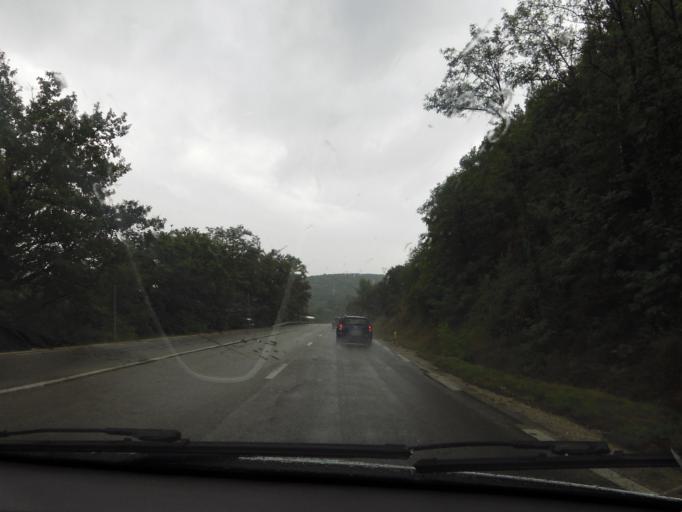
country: FR
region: Languedoc-Roussillon
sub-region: Departement du Gard
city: Les Salles-du-Gardon
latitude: 44.1872
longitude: 4.0451
